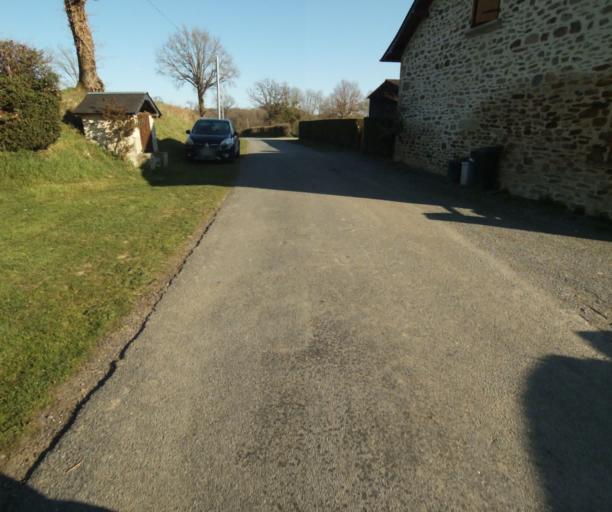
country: FR
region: Limousin
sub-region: Departement de la Correze
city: Chamboulive
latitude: 45.4625
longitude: 1.7350
